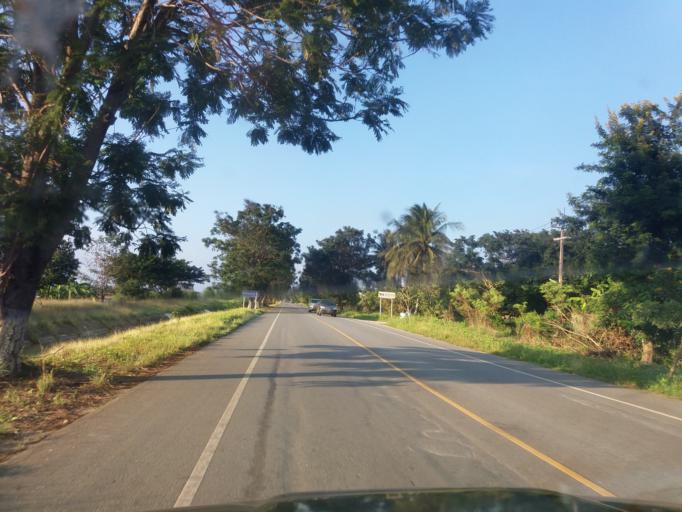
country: TH
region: Suphan Buri
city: Doem Bang Nang Buat
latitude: 14.8733
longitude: 100.0778
